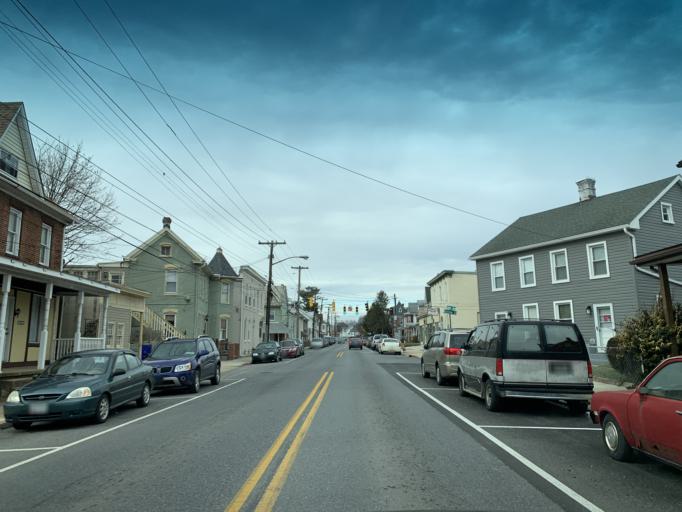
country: US
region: Maryland
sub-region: Washington County
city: Hagerstown
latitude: 39.6486
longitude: -77.7256
